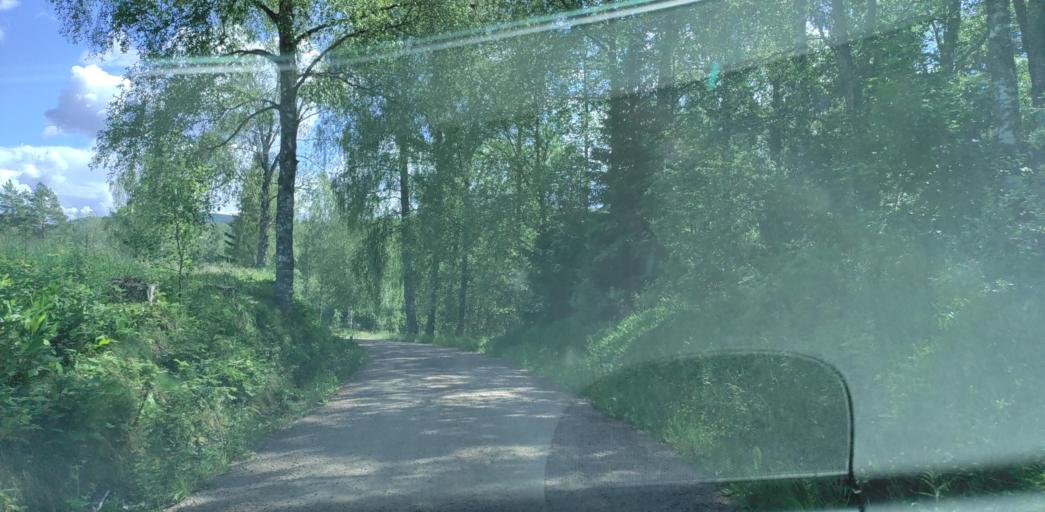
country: SE
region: Vaermland
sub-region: Munkfors Kommun
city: Munkfors
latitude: 59.9500
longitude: 13.4955
